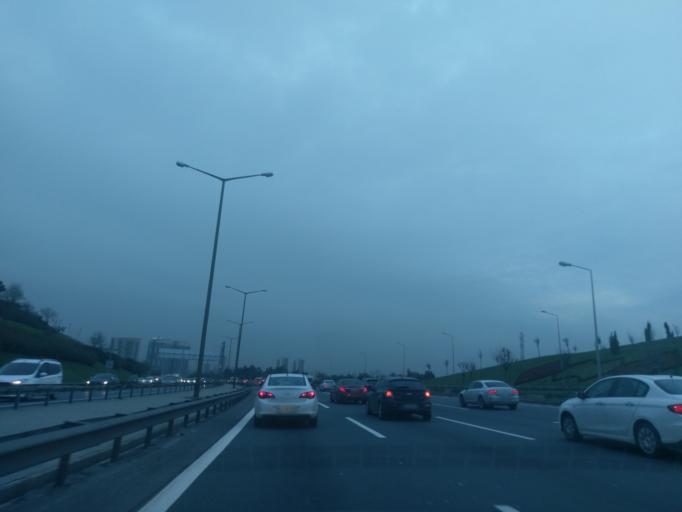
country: TR
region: Istanbul
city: Sisli
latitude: 41.0982
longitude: 28.9546
